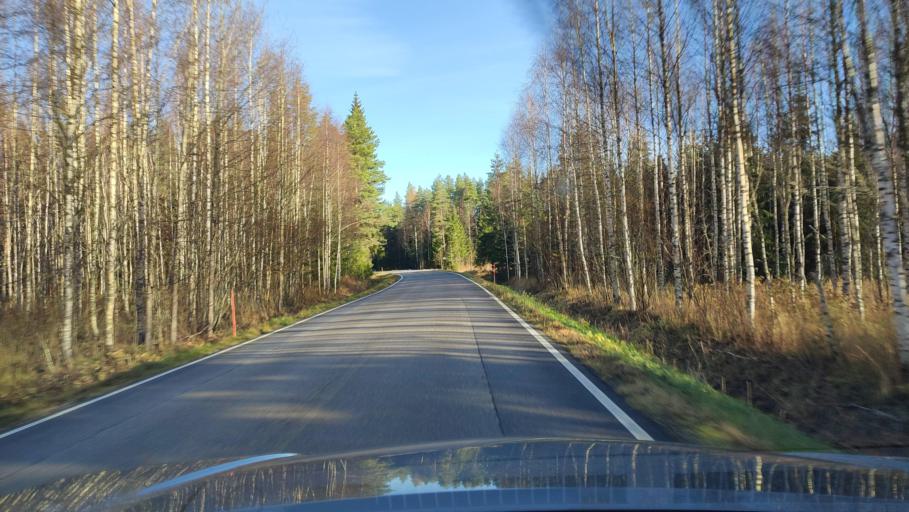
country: FI
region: Southern Ostrobothnia
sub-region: Suupohja
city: Teuva
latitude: 62.4160
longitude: 21.7066
